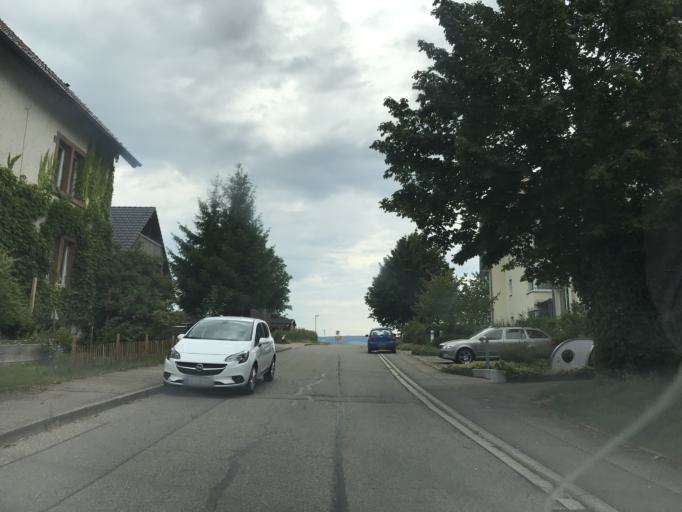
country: DE
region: Baden-Wuerttemberg
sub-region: Freiburg Region
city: Sankt Peter
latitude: 48.0139
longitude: 8.0341
